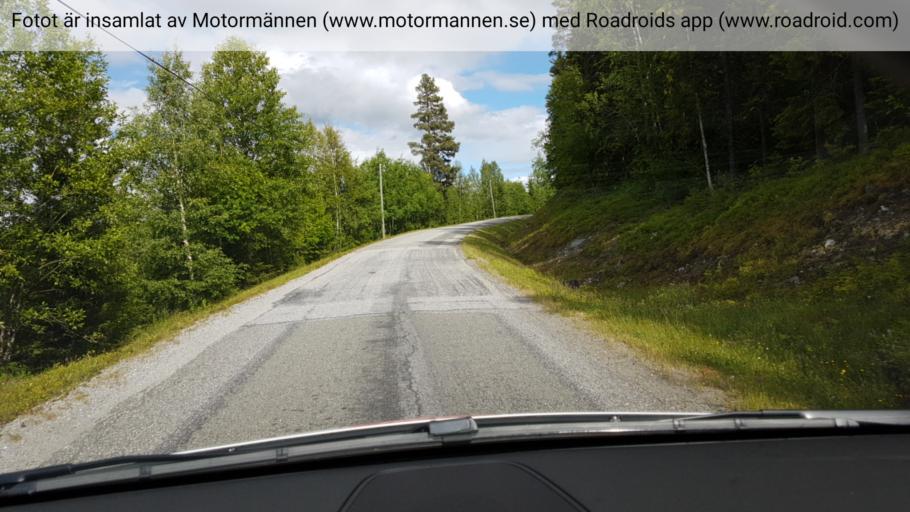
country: SE
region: Vaesterbotten
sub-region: Dorotea Kommun
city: Dorotea
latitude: 64.1275
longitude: 16.2903
